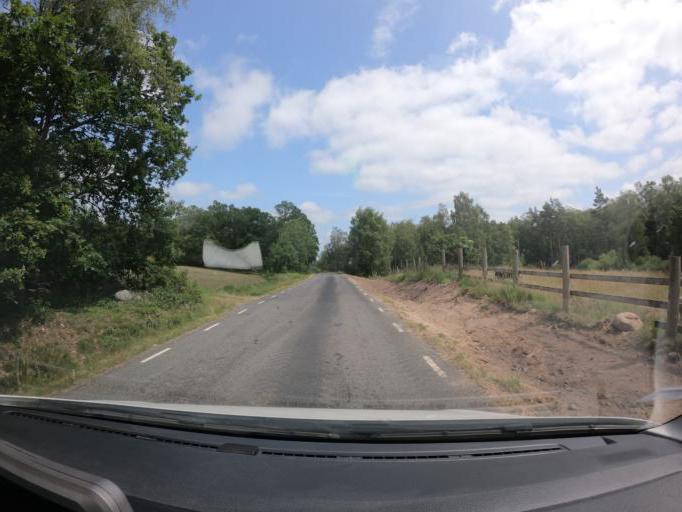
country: SE
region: Skane
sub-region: Hassleholms Kommun
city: Sosdala
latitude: 56.0542
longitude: 13.6172
